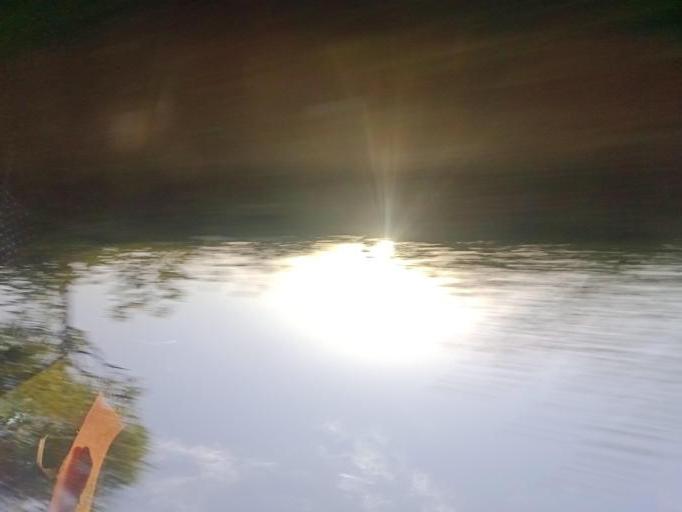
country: IE
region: Leinster
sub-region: Kilkenny
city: Castlecomer
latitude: 52.7319
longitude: -7.2369
